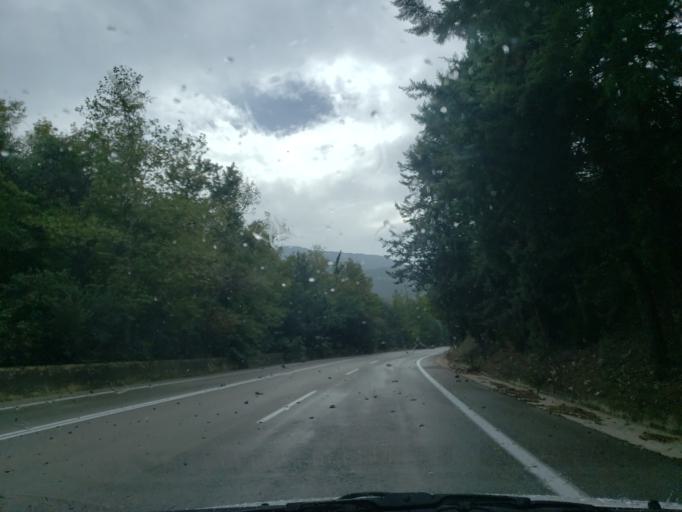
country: GR
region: Central Greece
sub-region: Nomos Fthiotidos
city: Anthili
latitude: 38.7876
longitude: 22.4938
